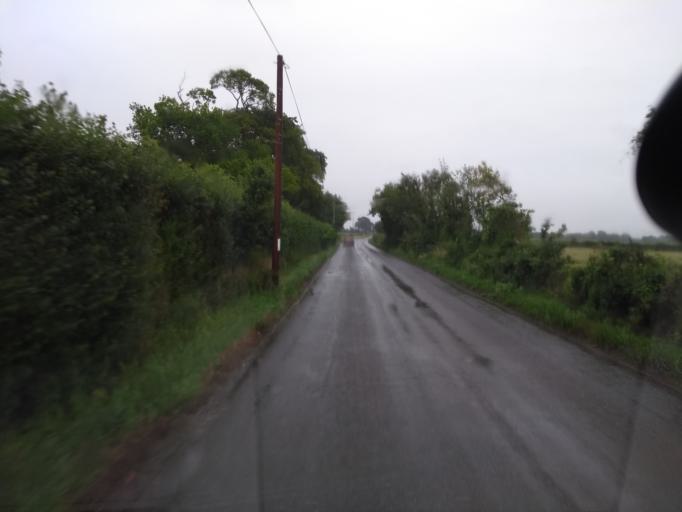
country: GB
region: England
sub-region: Somerset
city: Ilchester
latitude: 51.0753
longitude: -2.6862
